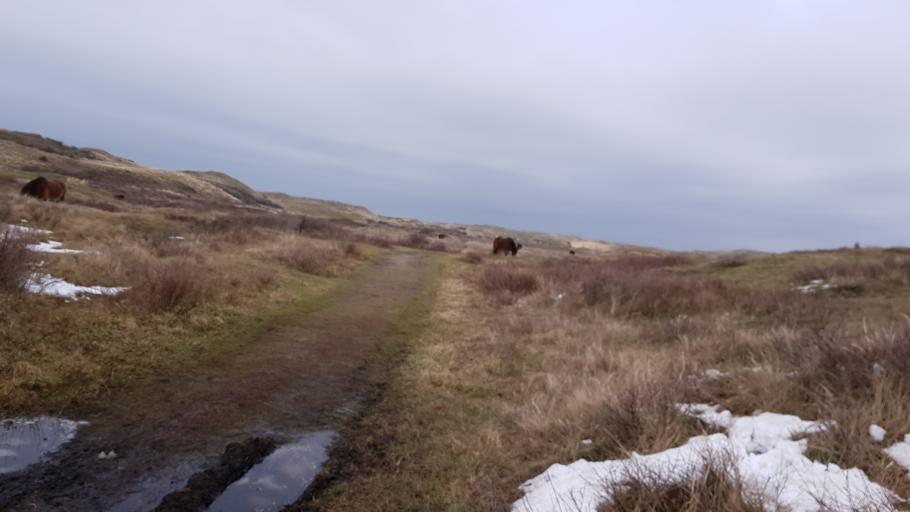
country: NL
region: North Holland
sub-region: Gemeente Bergen
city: Egmond aan Zee
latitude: 52.5813
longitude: 4.6164
